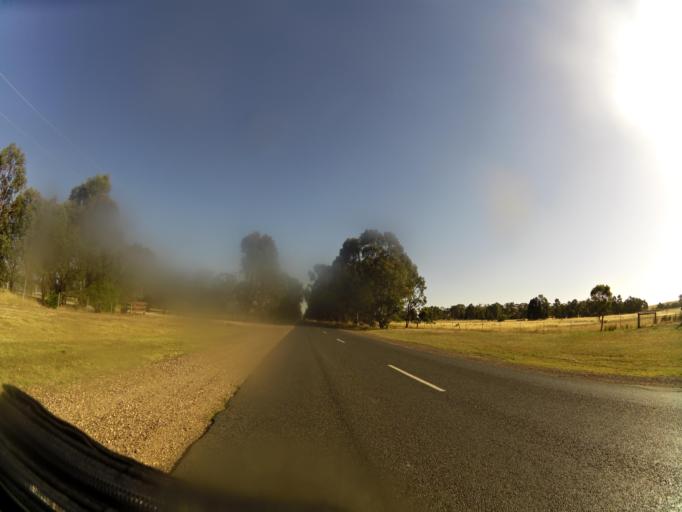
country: AU
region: Victoria
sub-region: Murrindindi
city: Kinglake West
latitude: -36.9872
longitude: 145.1118
